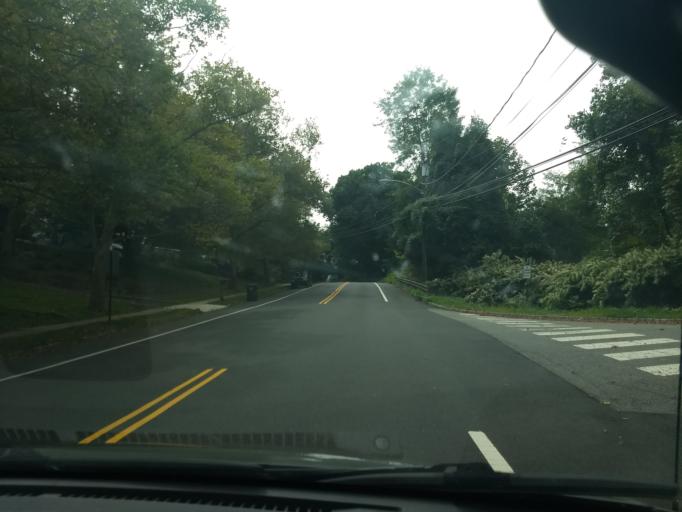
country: US
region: New Jersey
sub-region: Morris County
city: Morristown
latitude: 40.8082
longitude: -74.5071
